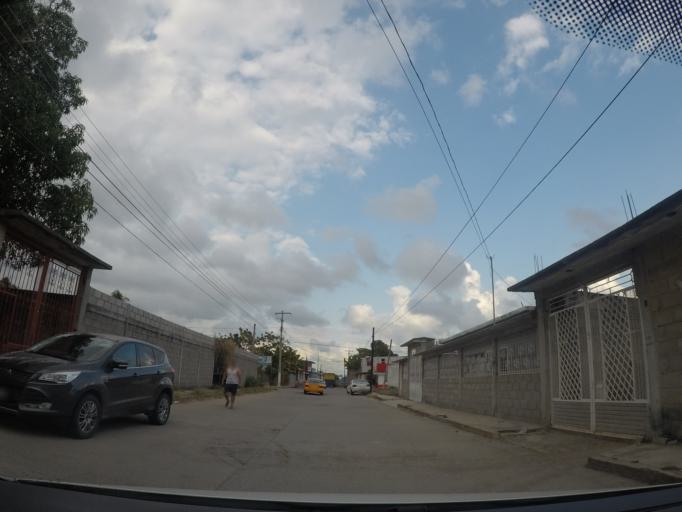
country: MX
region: Oaxaca
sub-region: Salina Cruz
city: Salina Cruz
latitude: 16.2136
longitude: -95.1971
